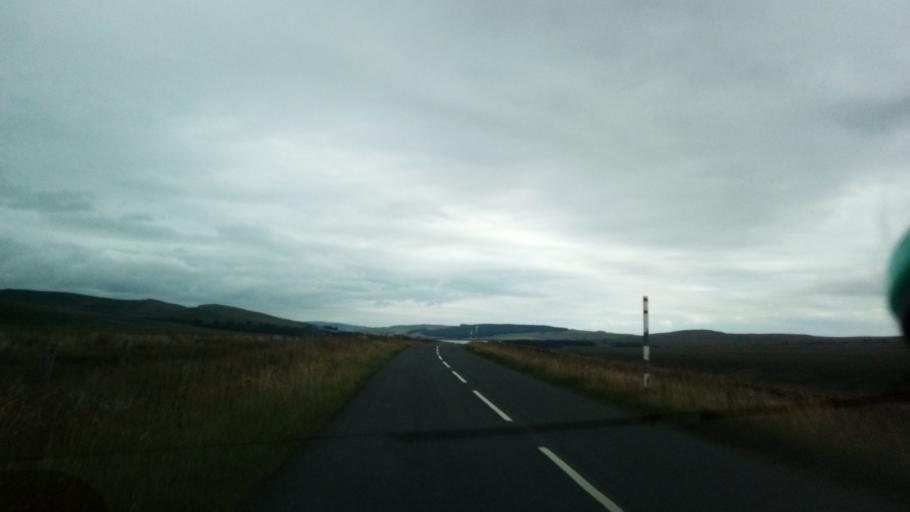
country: GB
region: England
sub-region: County Durham
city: Holwick
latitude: 54.5862
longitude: -2.1942
